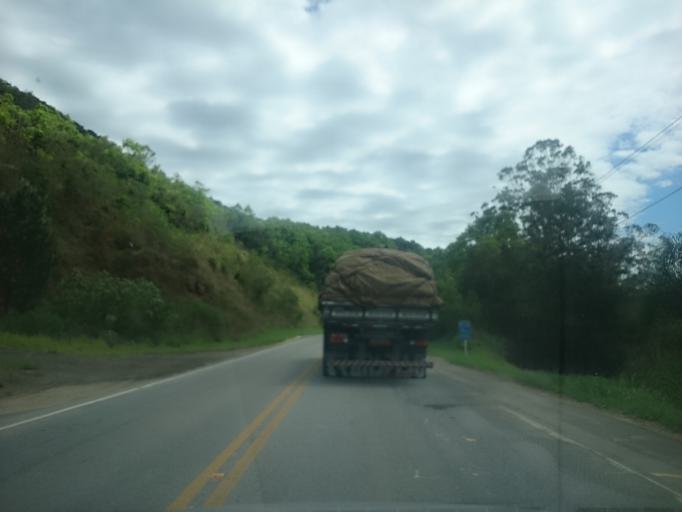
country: BR
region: Santa Catarina
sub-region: Anitapolis
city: Anitapolis
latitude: -27.6946
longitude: -49.3137
